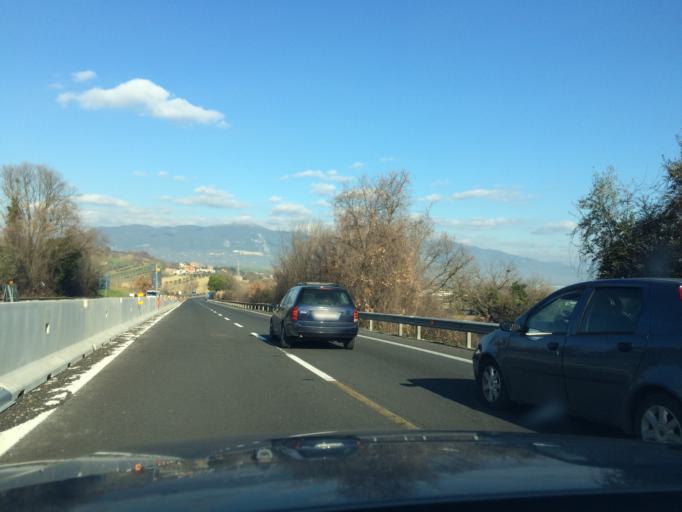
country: IT
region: Umbria
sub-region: Provincia di Terni
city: Narni Scalo
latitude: 42.5444
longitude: 12.5193
